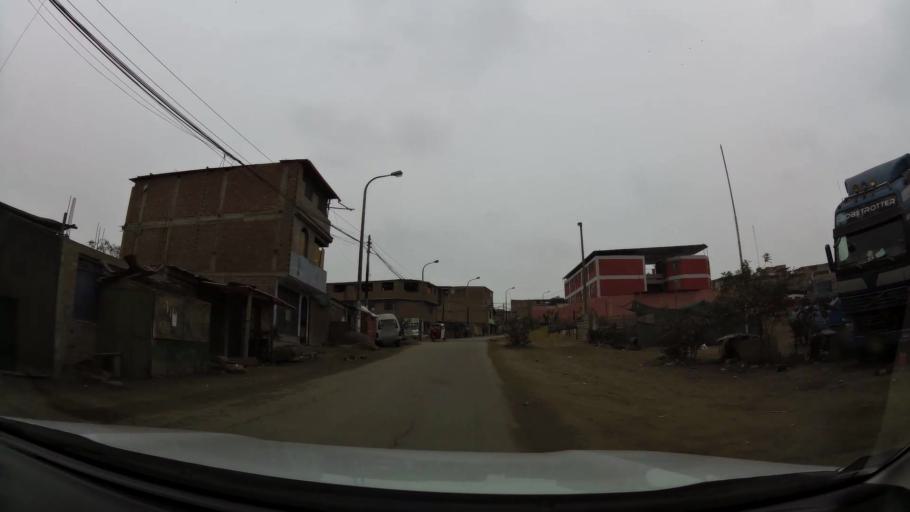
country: PE
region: Lima
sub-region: Lima
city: Surco
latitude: -12.2202
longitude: -76.9173
